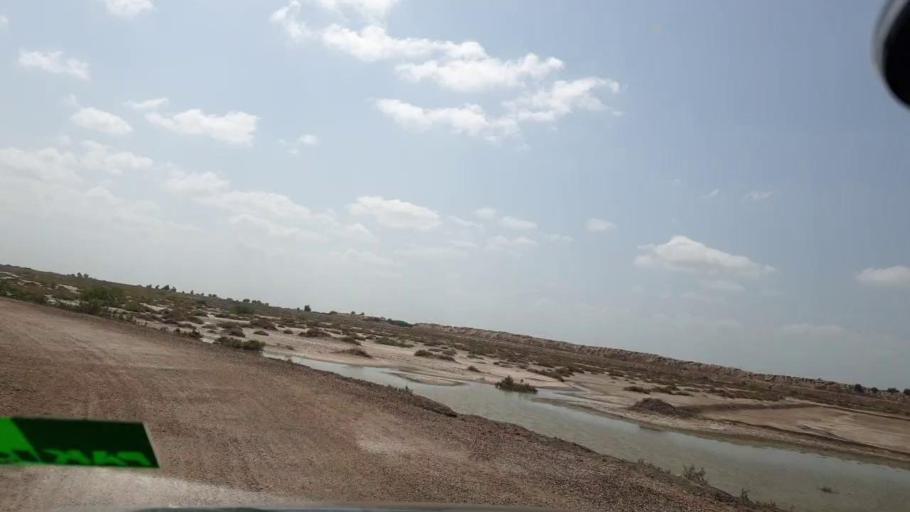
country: PK
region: Sindh
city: Kadhan
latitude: 24.5987
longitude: 69.1834
